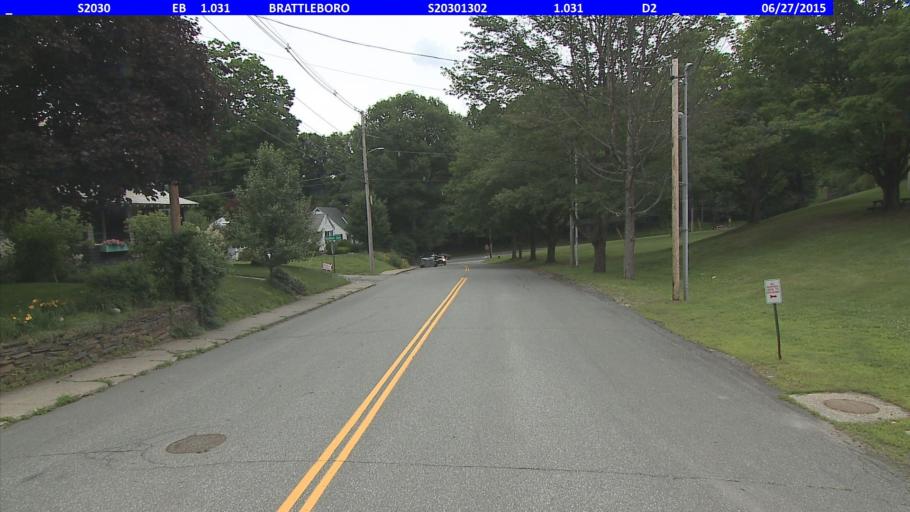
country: US
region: Vermont
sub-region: Windham County
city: Brattleboro
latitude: 42.8442
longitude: -72.5647
